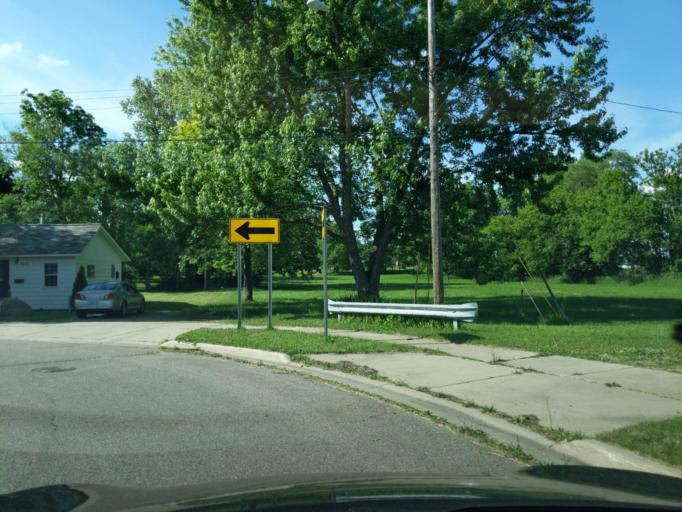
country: US
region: Michigan
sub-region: Ingham County
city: Lansing
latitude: 42.7562
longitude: -84.5347
